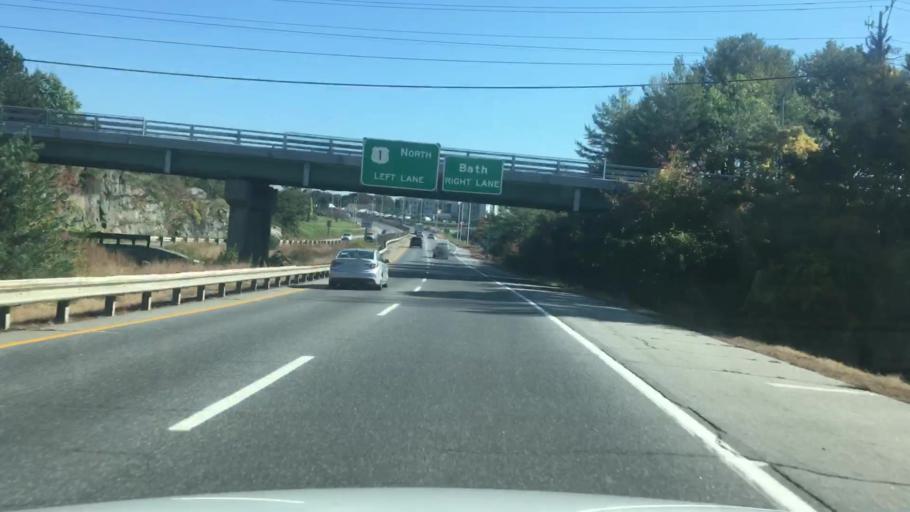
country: US
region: Maine
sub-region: Sagadahoc County
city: Bath
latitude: 43.9071
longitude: -69.8335
